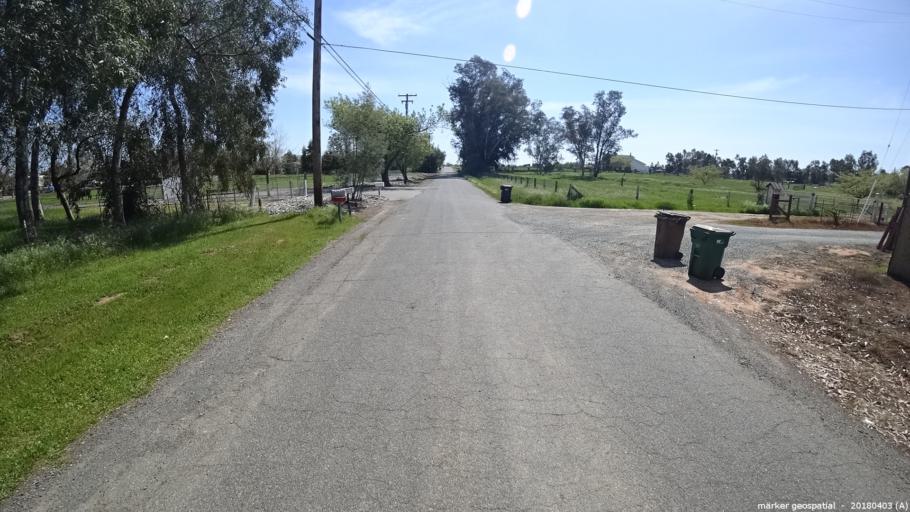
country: US
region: California
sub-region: Sacramento County
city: Clay
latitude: 38.3461
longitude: -121.2146
